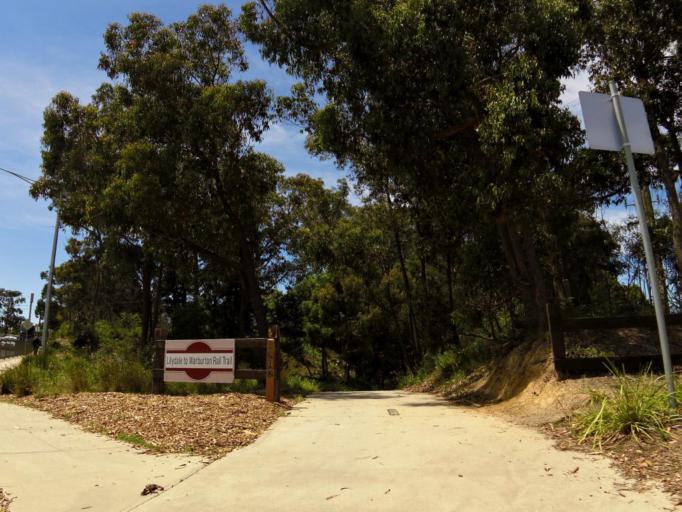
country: AU
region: Victoria
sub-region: Yarra Ranges
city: Mount Evelyn
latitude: -37.7869
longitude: 145.3805
